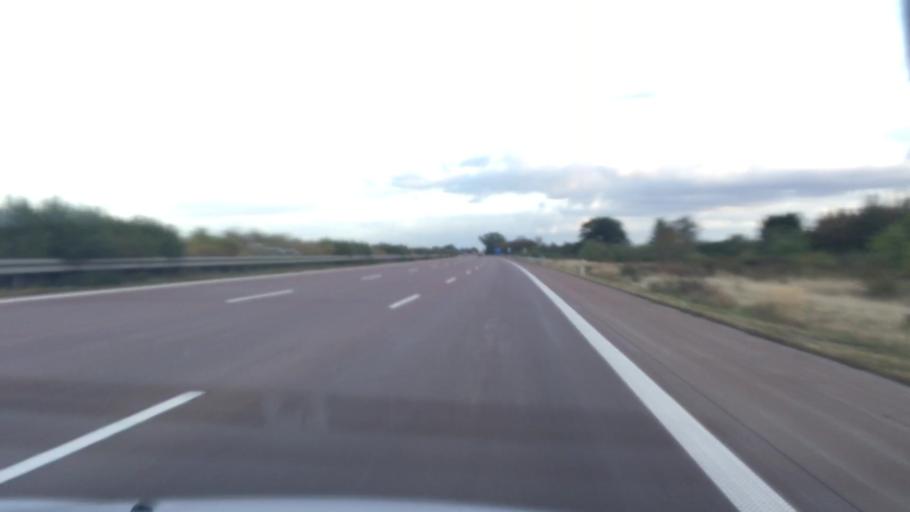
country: DE
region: Saxony-Anhalt
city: Grobers
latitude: 51.4602
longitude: 12.1007
